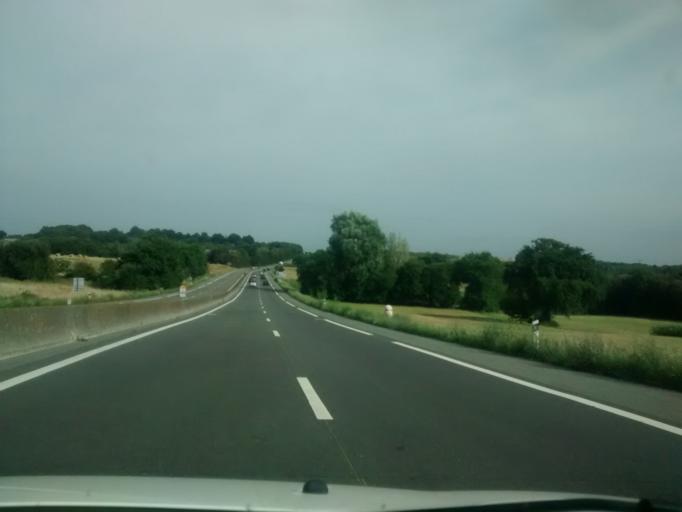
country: FR
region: Brittany
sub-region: Departement d'Ille-et-Vilaine
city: Saint-Pere
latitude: 48.5738
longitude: -1.9383
